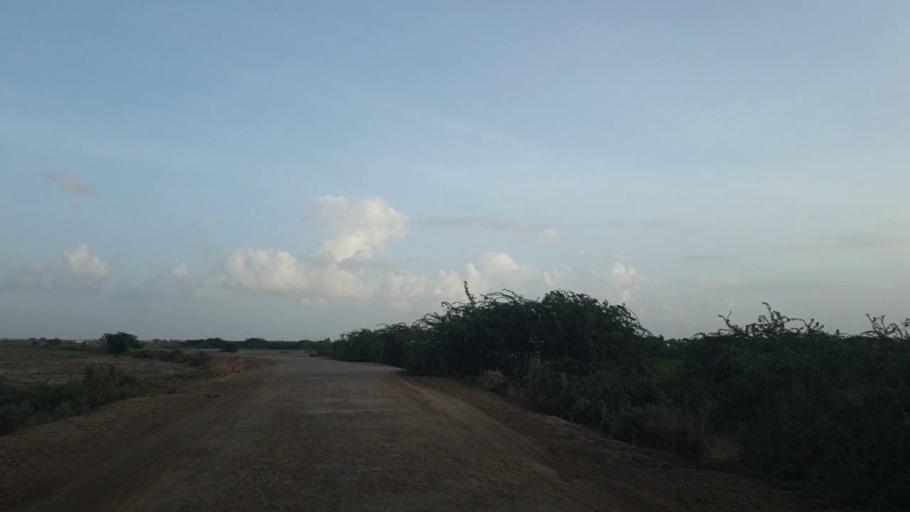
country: PK
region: Sindh
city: Kadhan
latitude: 24.5584
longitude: 69.1215
